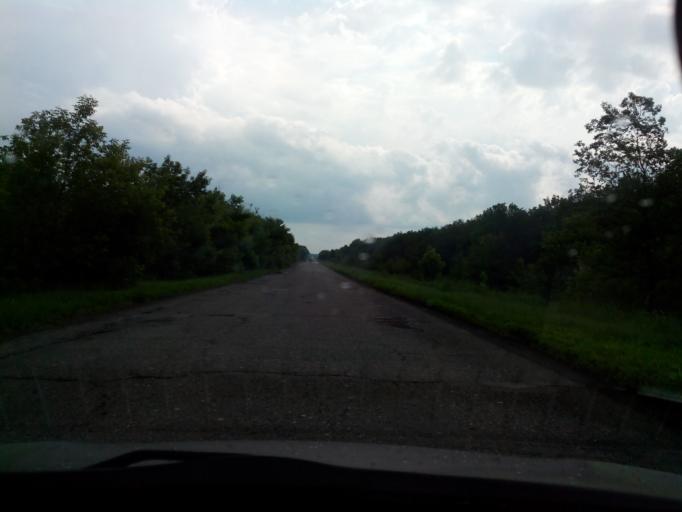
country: RU
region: Volgograd
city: Kumylzhenskaya
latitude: 49.9075
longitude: 42.9303
